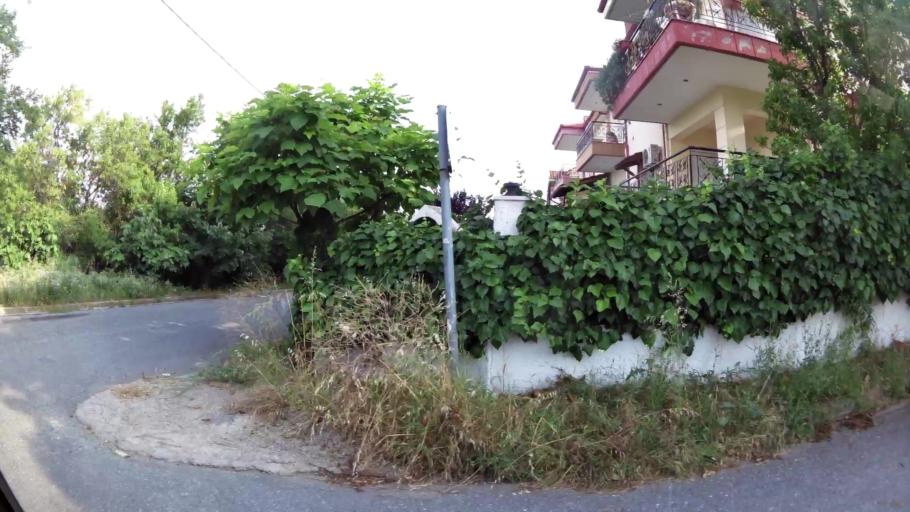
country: GR
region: Central Macedonia
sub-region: Nomos Thessalonikis
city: Oraiokastro
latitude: 40.7202
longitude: 22.9028
